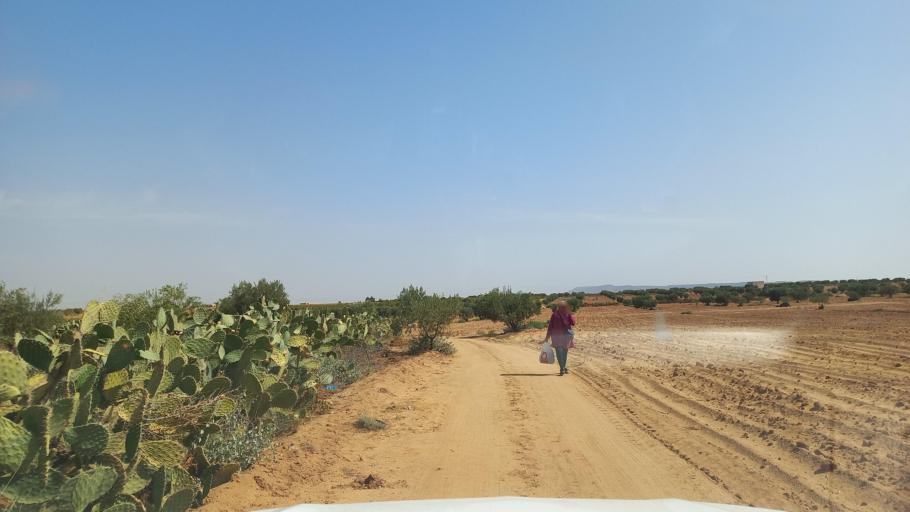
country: TN
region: Al Qasrayn
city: Kasserine
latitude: 35.2416
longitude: 9.0591
